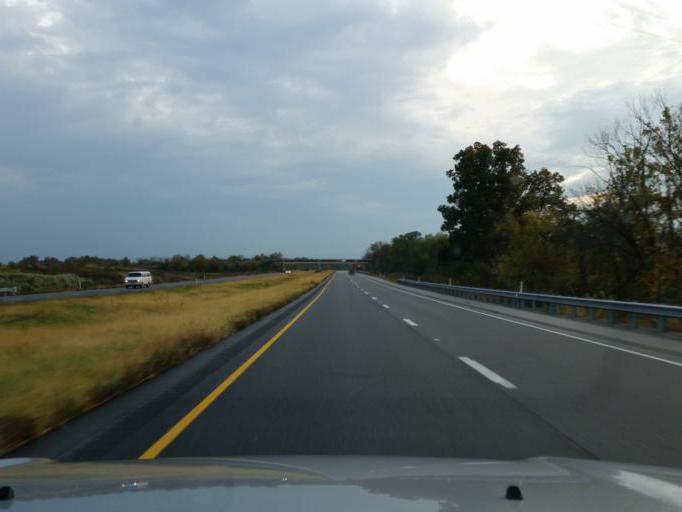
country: US
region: Pennsylvania
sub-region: Adams County
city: Biglerville
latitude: 39.9148
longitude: -77.1642
